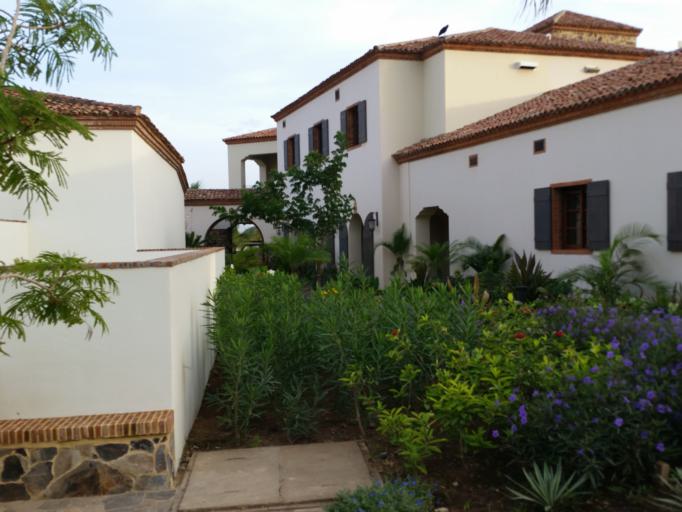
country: NI
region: Rivas
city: Tola
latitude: 11.4414
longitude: -86.0854
